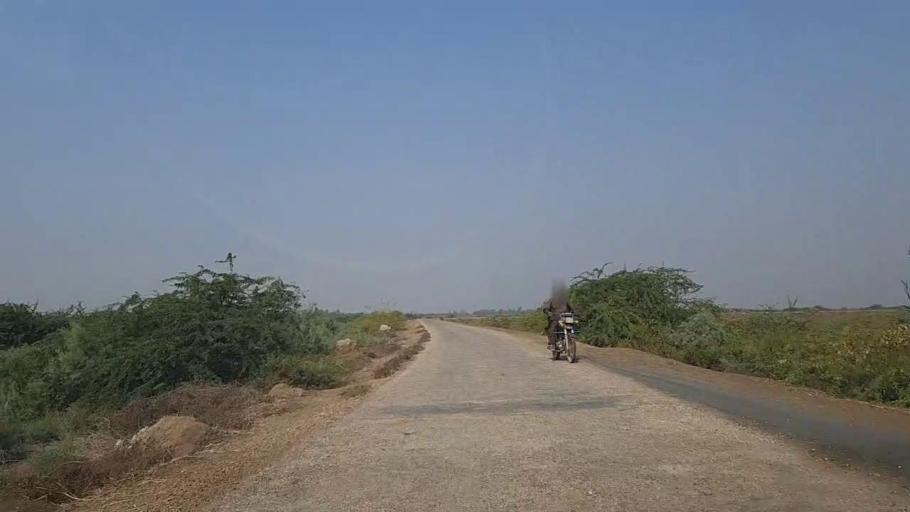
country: PK
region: Sindh
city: Keti Bandar
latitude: 24.2277
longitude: 67.6754
